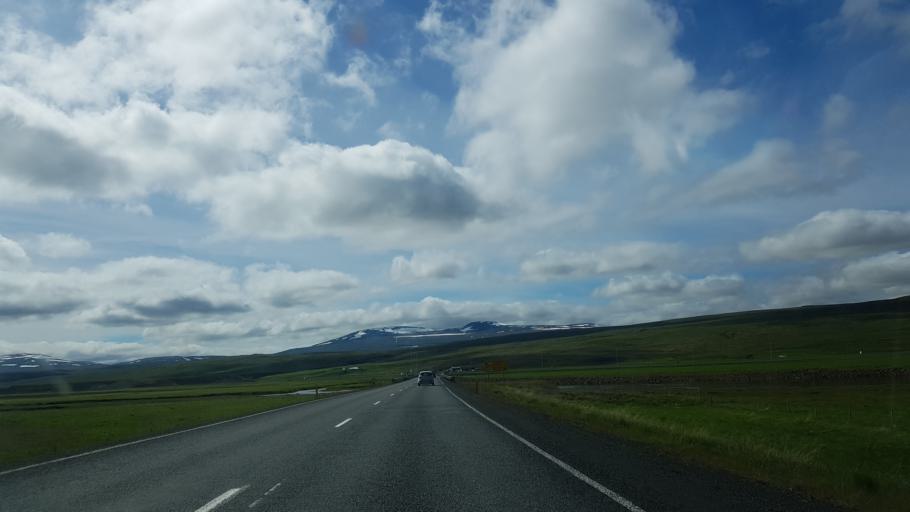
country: IS
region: West
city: Borgarnes
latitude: 65.1490
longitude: -21.0686
